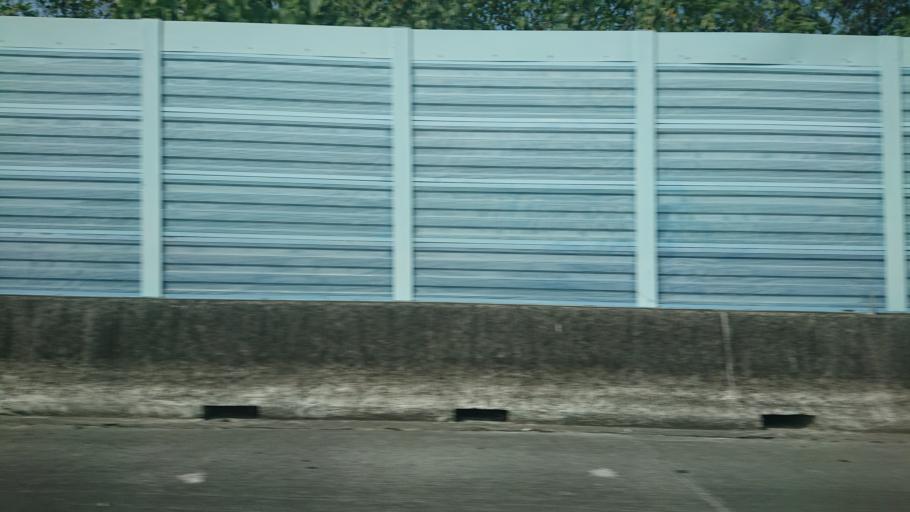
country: TW
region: Taiwan
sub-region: Nantou
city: Nantou
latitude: 23.8921
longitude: 120.7107
